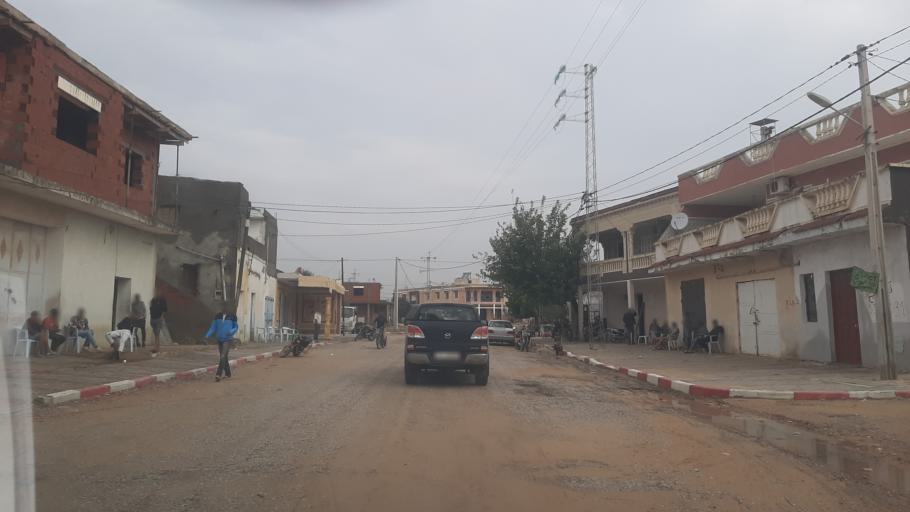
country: TN
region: Al Munastir
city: Sidi Bin Nur
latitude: 35.4806
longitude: 10.8732
